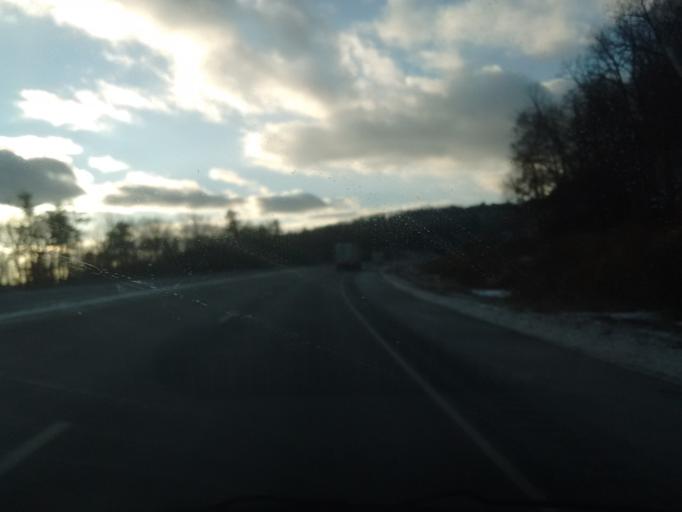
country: US
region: Pennsylvania
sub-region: Pike County
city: Milford
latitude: 41.3406
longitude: -74.7748
